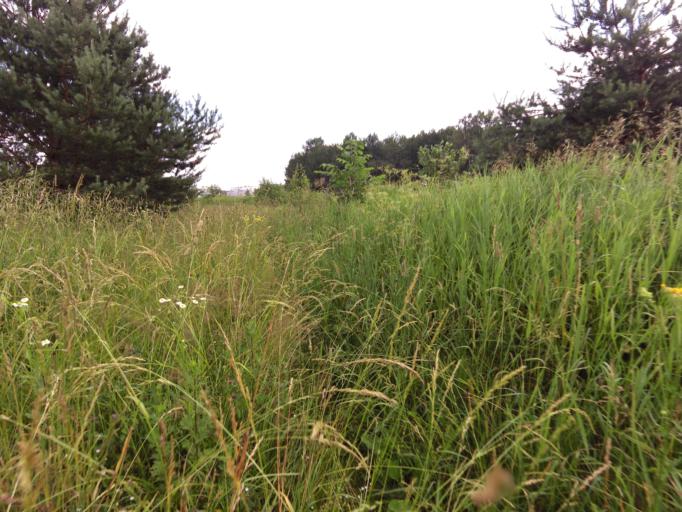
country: LT
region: Vilnius County
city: Pasilaiciai
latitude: 54.7530
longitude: 25.2234
